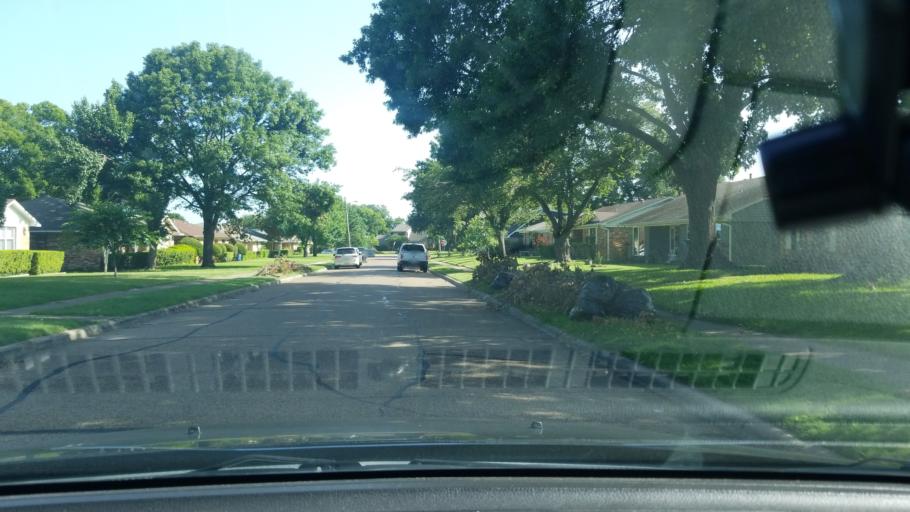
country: US
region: Texas
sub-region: Dallas County
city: Mesquite
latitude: 32.8088
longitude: -96.6803
